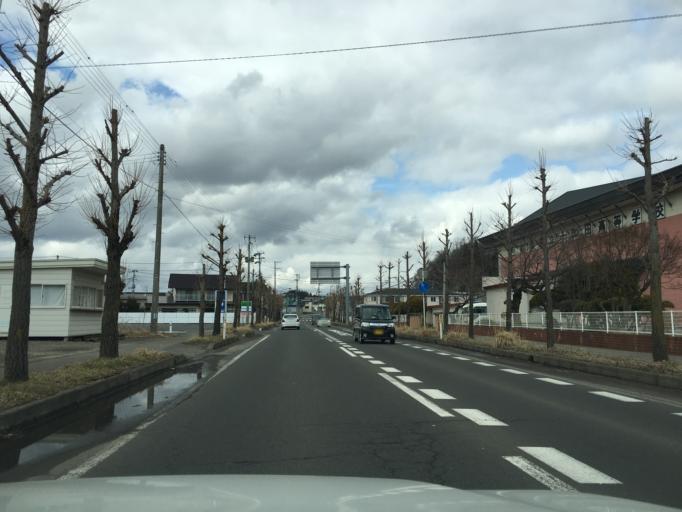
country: JP
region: Akita
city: Hanawa
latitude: 40.2661
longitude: 140.7698
